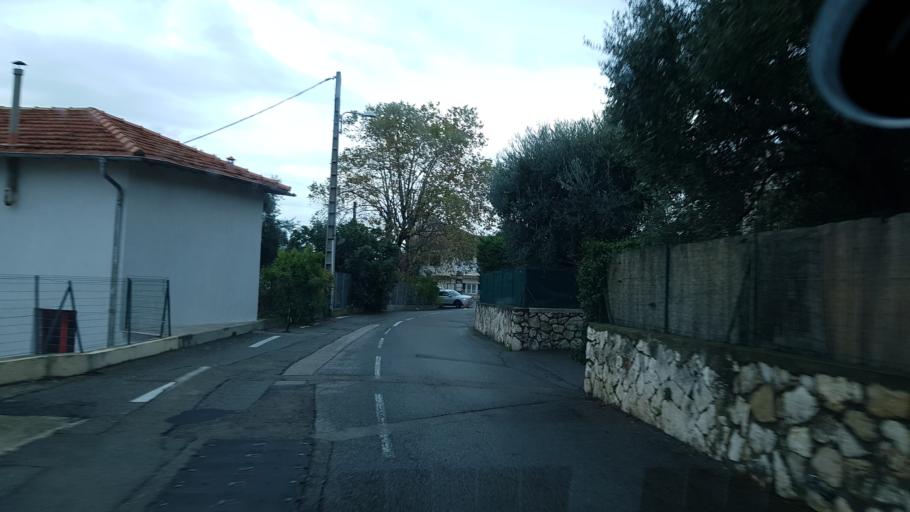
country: FR
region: Provence-Alpes-Cote d'Azur
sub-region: Departement des Alpes-Maritimes
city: Nice
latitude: 43.6979
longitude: 7.2369
